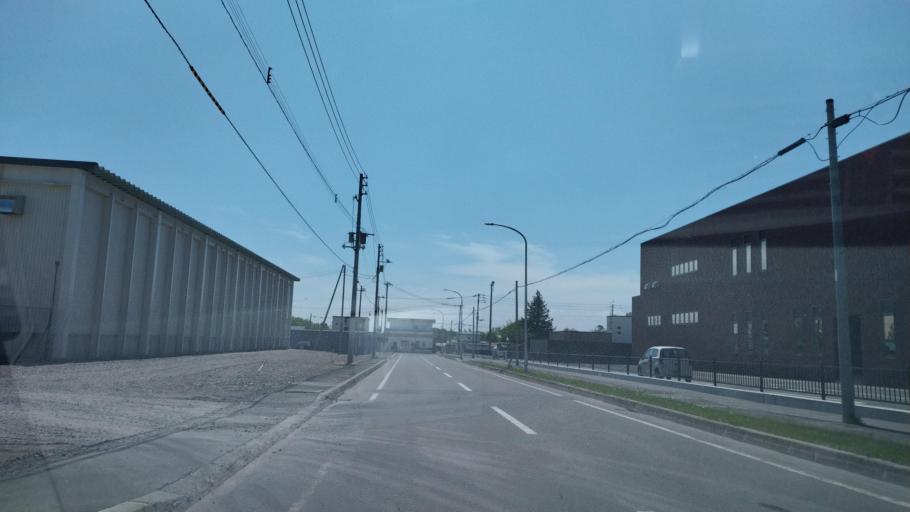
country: JP
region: Hokkaido
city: Otofuke
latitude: 43.1636
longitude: 143.2470
